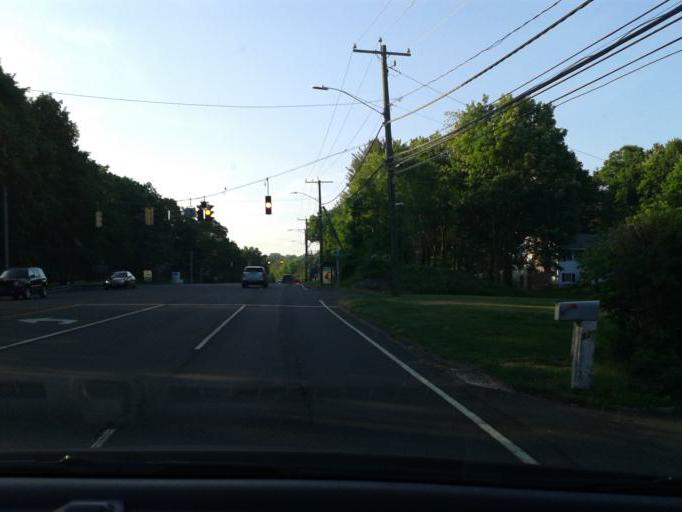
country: US
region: Connecticut
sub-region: Fairfield County
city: North Stamford
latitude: 41.0974
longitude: -73.5644
